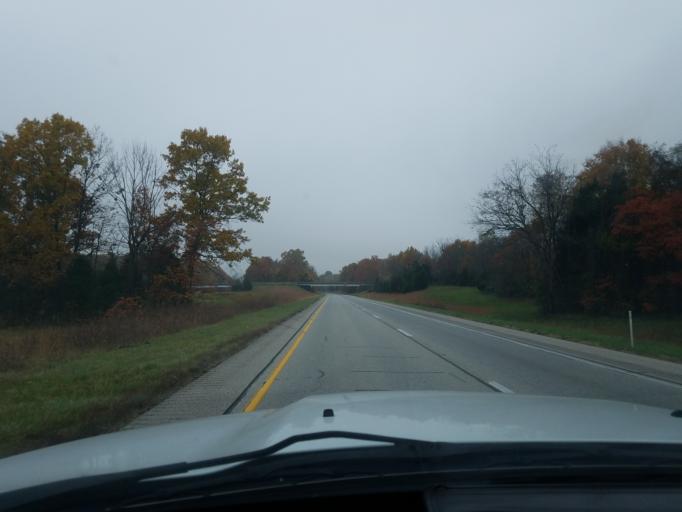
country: US
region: Indiana
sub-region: Floyd County
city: Georgetown
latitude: 38.2521
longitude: -86.0477
